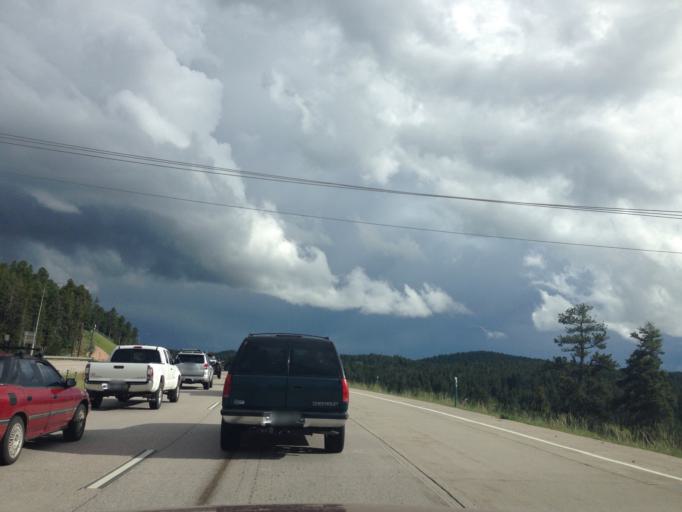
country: US
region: Colorado
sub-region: Jefferson County
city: Evergreen
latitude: 39.5276
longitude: -105.3076
